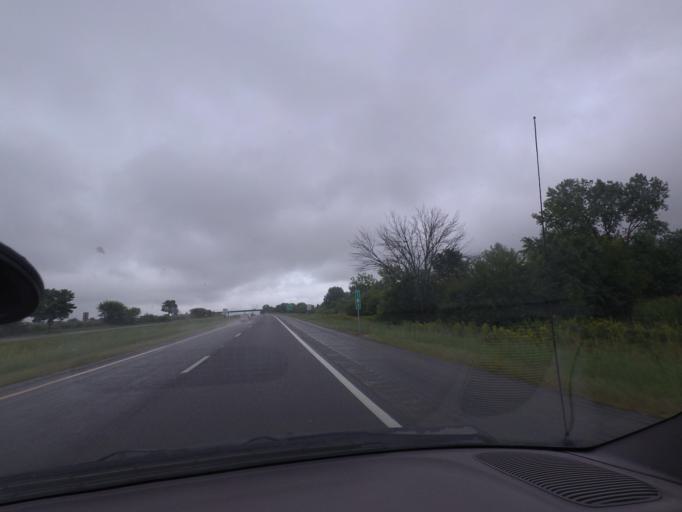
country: US
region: Illinois
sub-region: Champaign County
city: Champaign
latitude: 40.1202
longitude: -88.3197
